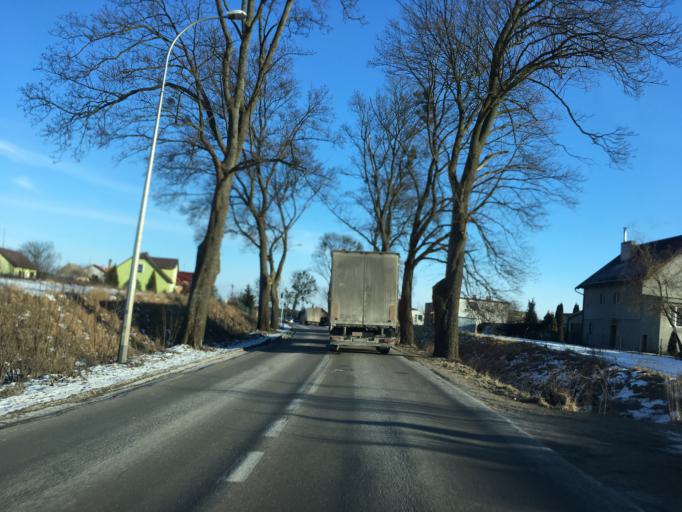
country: PL
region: Pomeranian Voivodeship
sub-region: Powiat starogardzki
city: Zblewo
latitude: 53.9425
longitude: 18.3174
